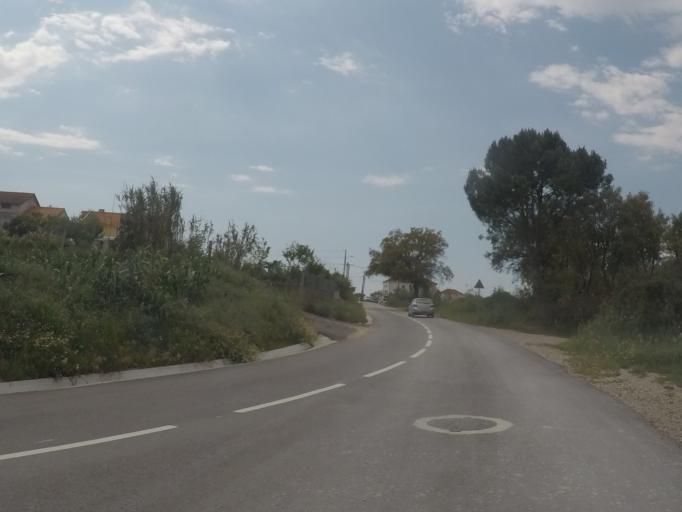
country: PT
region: Setubal
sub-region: Sesimbra
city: Sesimbra
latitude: 38.4609
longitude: -9.0682
